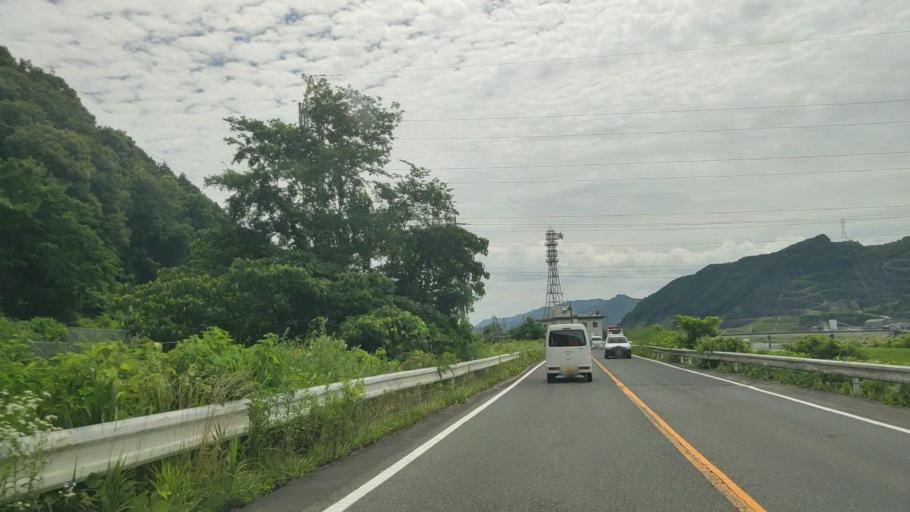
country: JP
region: Okayama
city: Tsuyama
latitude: 35.0831
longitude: 133.7249
